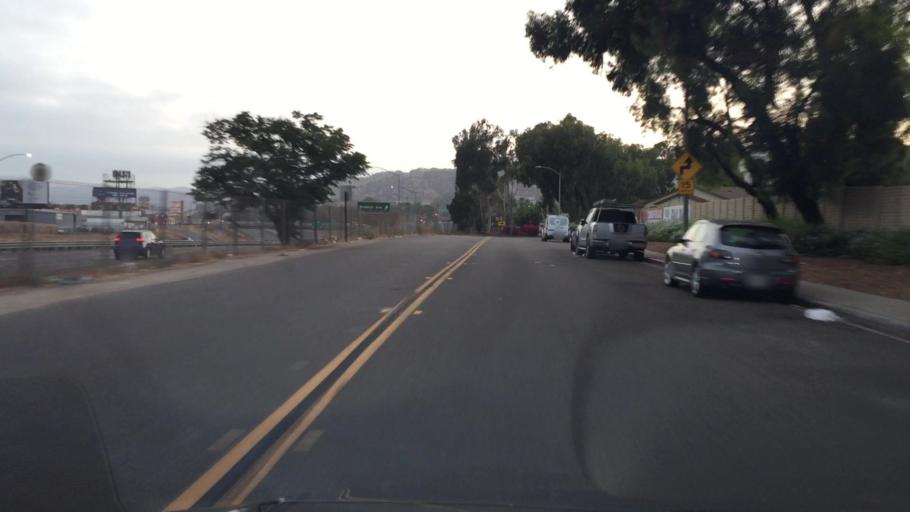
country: US
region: California
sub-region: San Diego County
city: El Cajon
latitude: 32.8152
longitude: -116.9609
